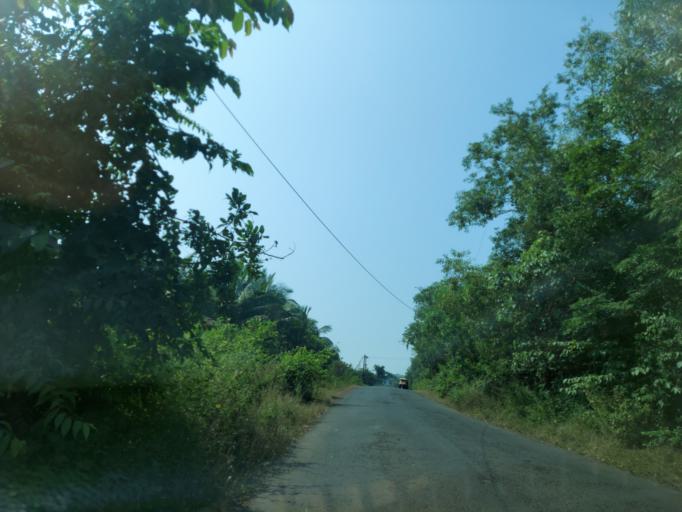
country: IN
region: Maharashtra
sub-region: Sindhudurg
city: Kudal
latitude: 15.9698
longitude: 73.6047
